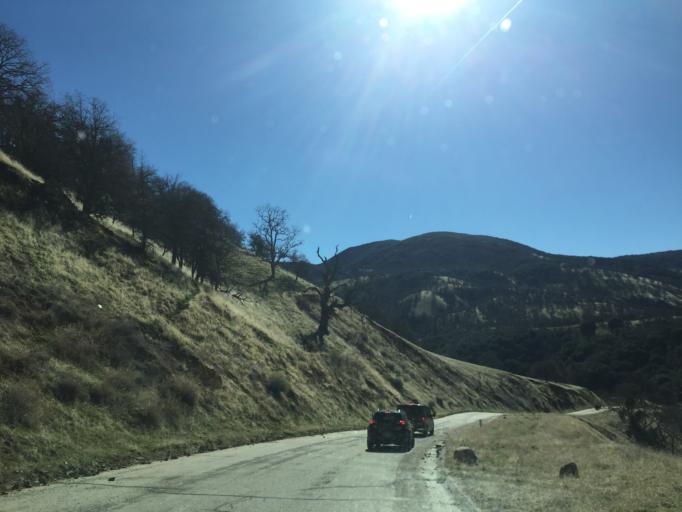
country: US
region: California
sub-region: Kern County
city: Lebec
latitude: 34.8885
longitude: -118.7826
